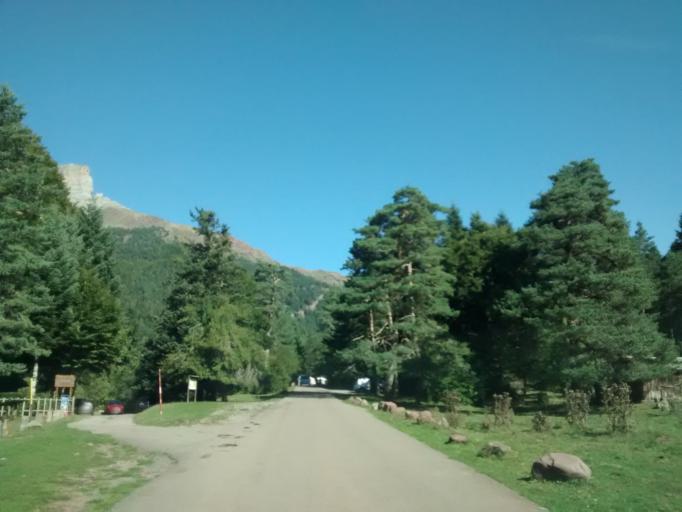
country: ES
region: Aragon
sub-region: Provincia de Huesca
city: Aragues del Puerto
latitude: 42.8326
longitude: -0.7109
